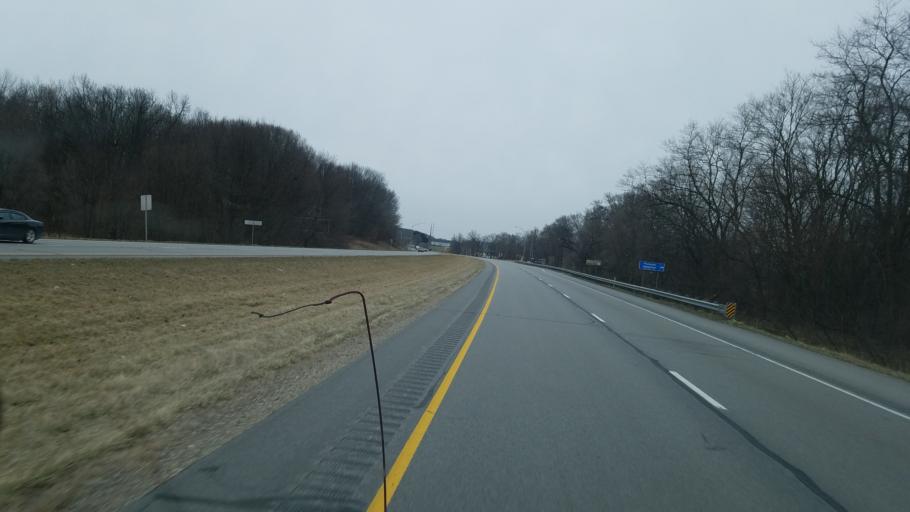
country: US
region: Indiana
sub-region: Marshall County
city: Plymouth
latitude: 41.3019
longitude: -86.2751
